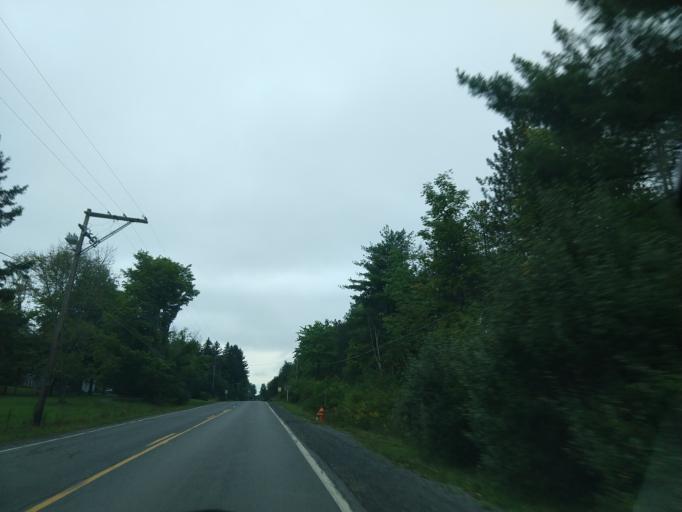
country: US
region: New York
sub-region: Tompkins County
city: South Hill
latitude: 42.4118
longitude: -76.4737
